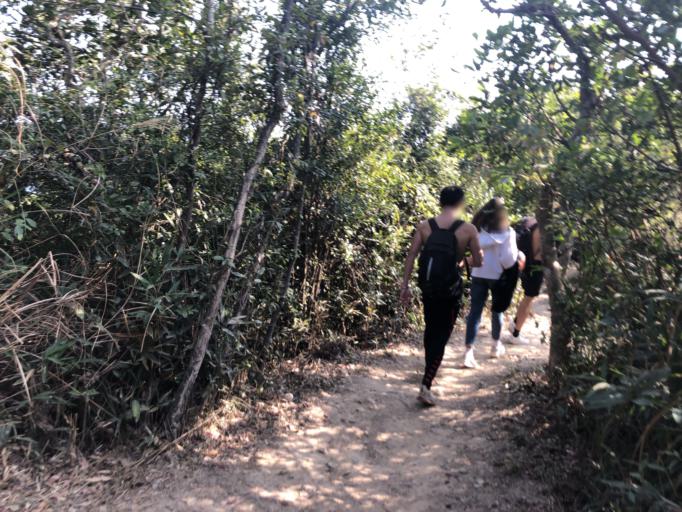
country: HK
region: Sai Kung
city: Sai Kung
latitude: 22.3650
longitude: 114.2918
